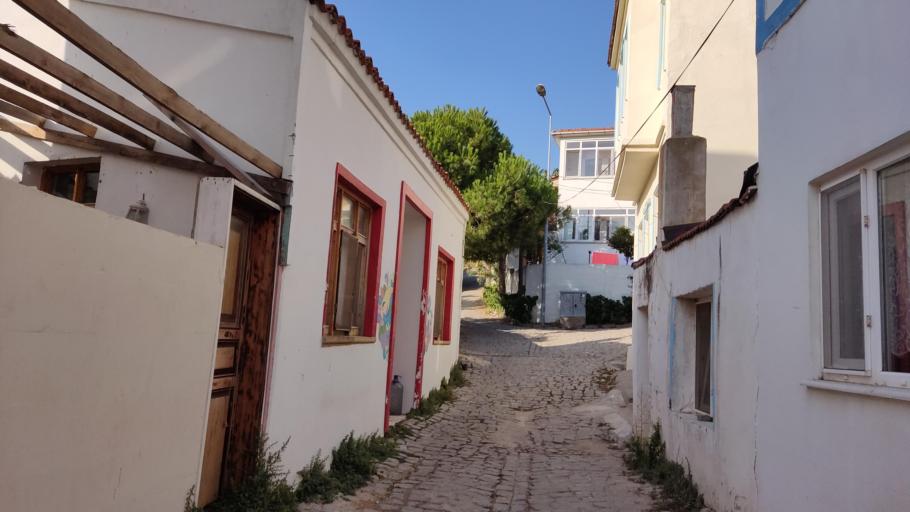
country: TR
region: Canakkale
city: Bozcaada
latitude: 39.8327
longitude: 26.0703
